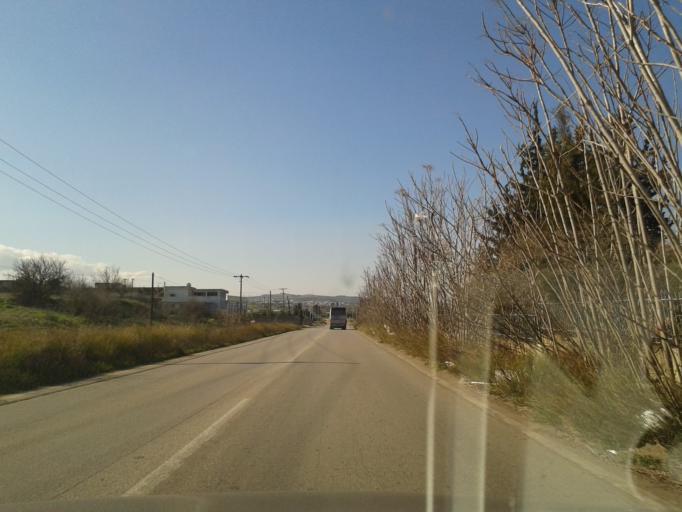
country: GR
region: Central Greece
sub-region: Nomos Voiotias
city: Thivai
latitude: 38.3404
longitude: 23.3537
